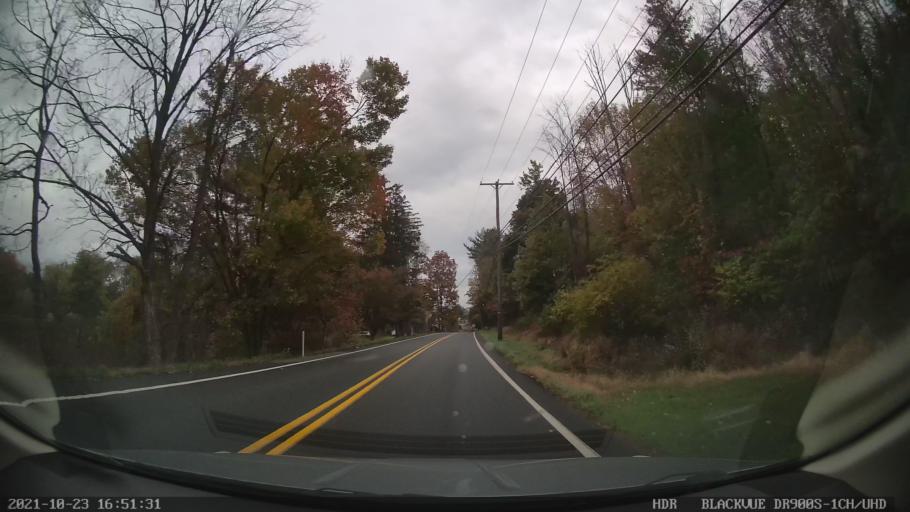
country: US
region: Pennsylvania
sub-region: Berks County
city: Red Lion
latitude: 40.4713
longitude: -75.6065
